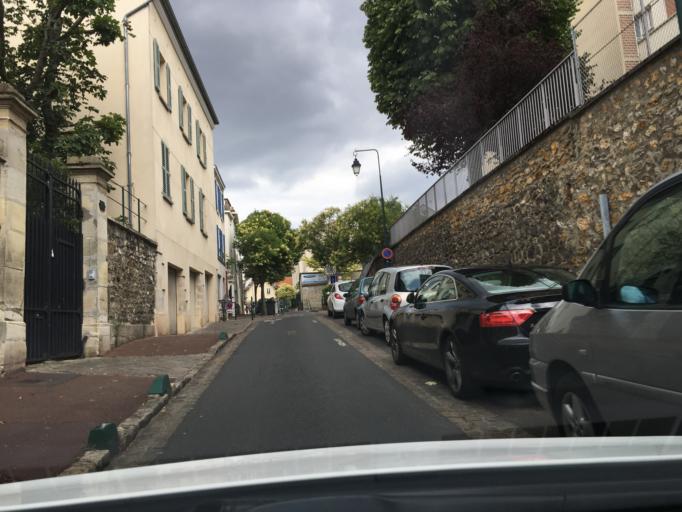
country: FR
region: Ile-de-France
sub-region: Departement des Hauts-de-Seine
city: Rueil-Malmaison
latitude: 48.8749
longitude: 2.1831
